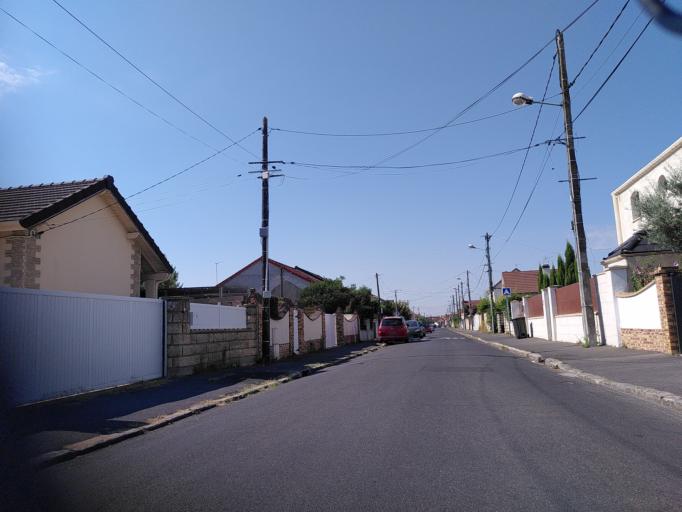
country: FR
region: Ile-de-France
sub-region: Departement de l'Essonne
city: Paray-Vieille-Poste
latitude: 48.7124
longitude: 2.3775
